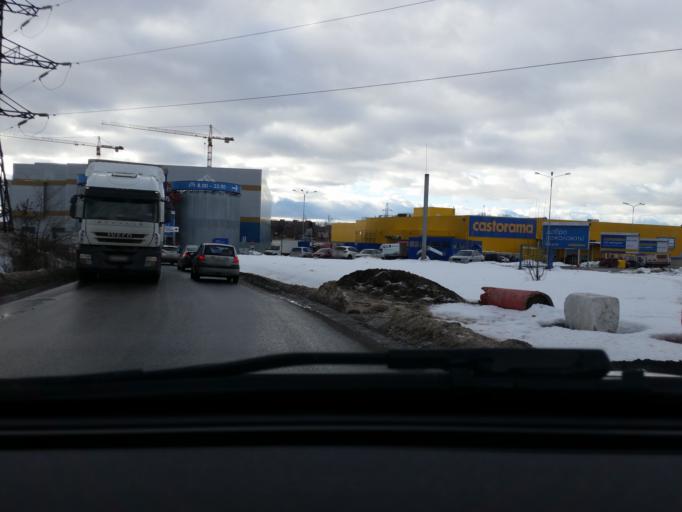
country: RU
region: Moskovskaya
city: Shcherbinka
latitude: 55.4945
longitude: 37.5753
